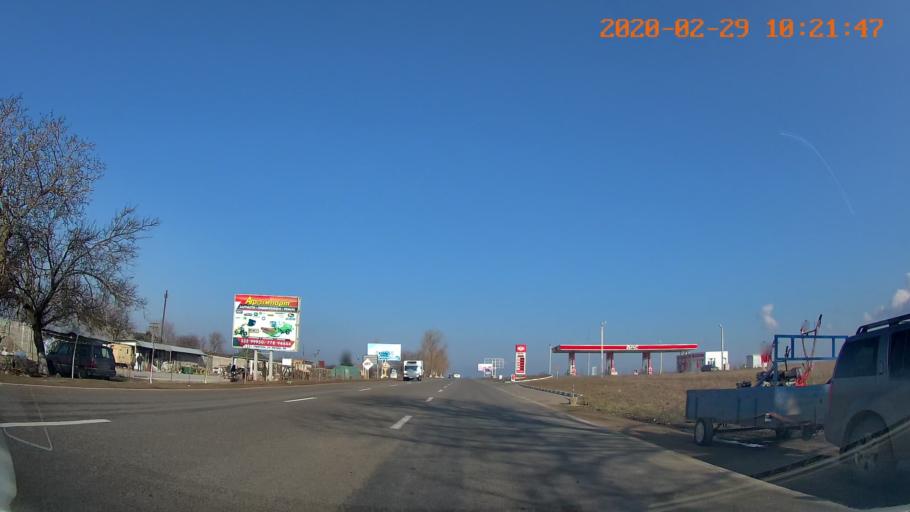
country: MD
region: Telenesti
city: Tiraspolul Nou
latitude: 46.8695
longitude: 29.6086
